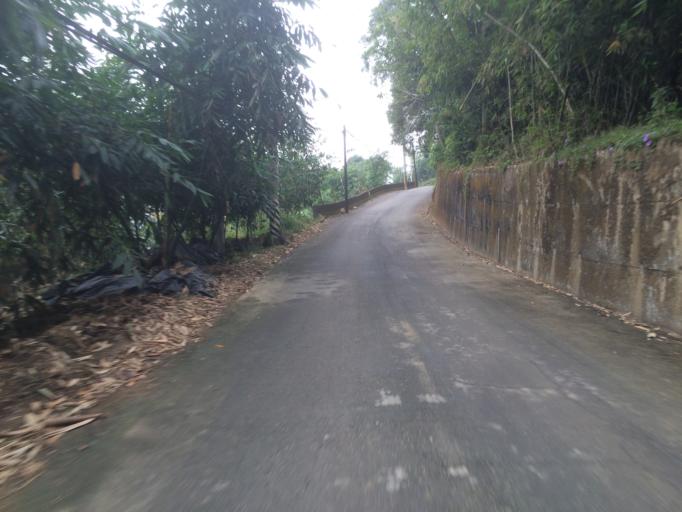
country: TW
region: Taiwan
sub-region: Taichung City
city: Taichung
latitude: 24.1608
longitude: 120.7627
